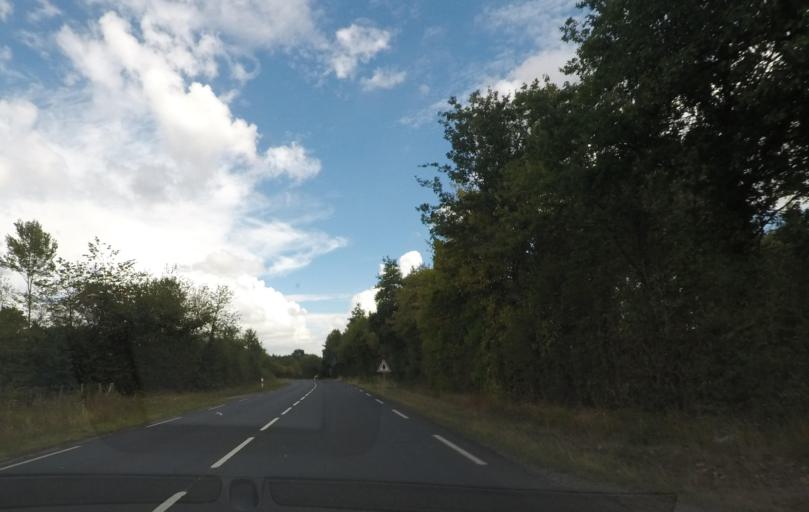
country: FR
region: Pays de la Loire
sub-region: Departement de la Sarthe
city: Champagne
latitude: 48.0596
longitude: 0.2915
